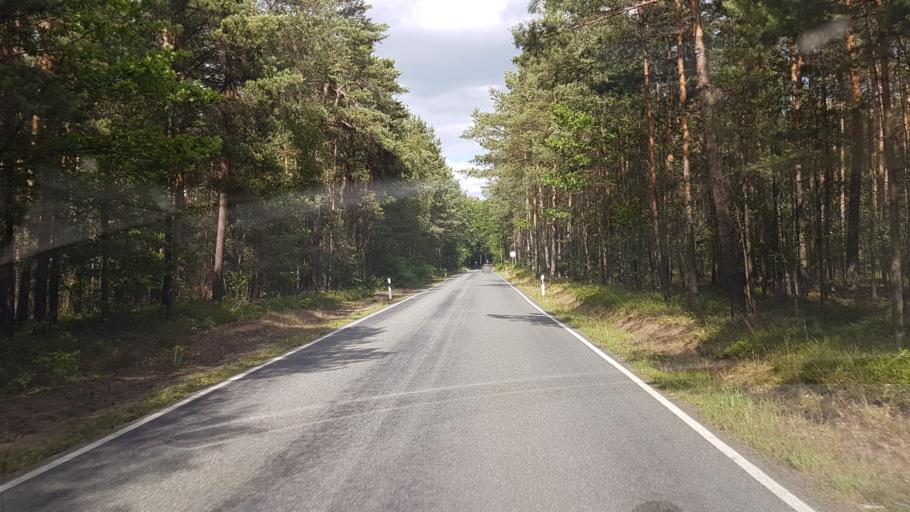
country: DE
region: Brandenburg
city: Guteborn
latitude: 51.4160
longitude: 13.9266
